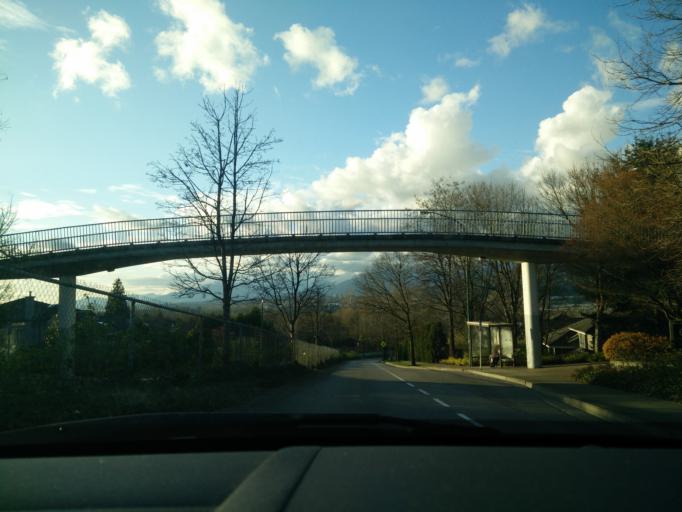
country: CA
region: British Columbia
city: New Westminster
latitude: 49.2366
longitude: -122.9056
